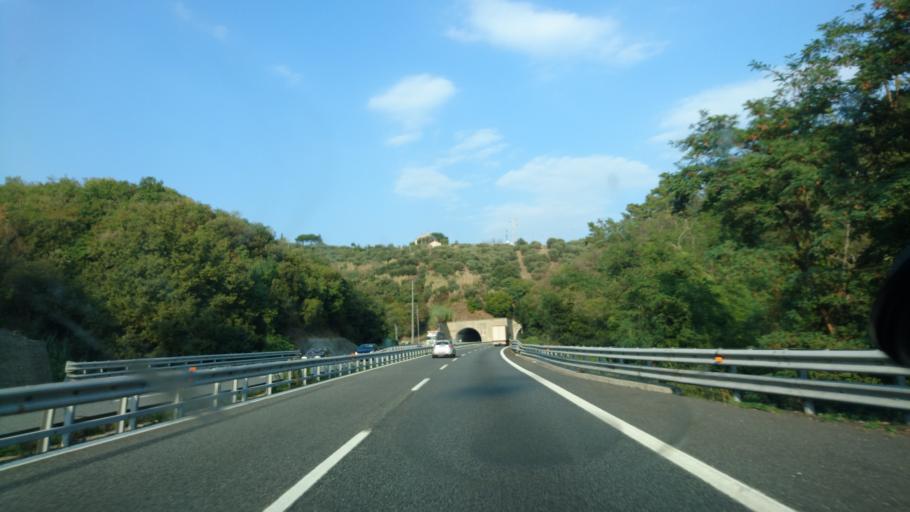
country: IT
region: Liguria
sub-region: Provincia di Savona
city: Savona
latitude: 44.3203
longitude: 8.4813
